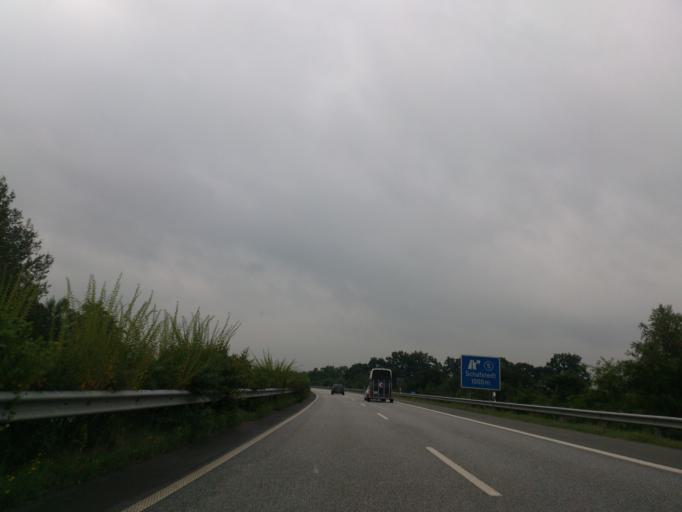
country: DE
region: Schleswig-Holstein
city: Schafstedt
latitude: 54.0825
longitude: 9.2693
